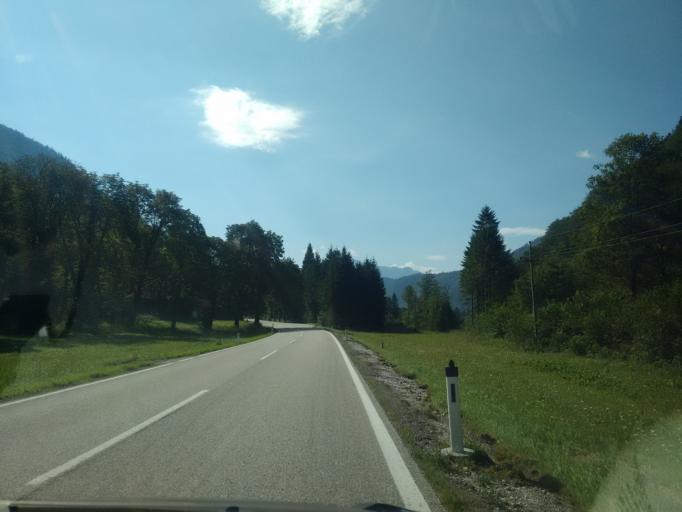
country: AT
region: Upper Austria
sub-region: Politischer Bezirk Gmunden
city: Gruenau im Almtal
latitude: 47.8199
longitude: 13.9507
